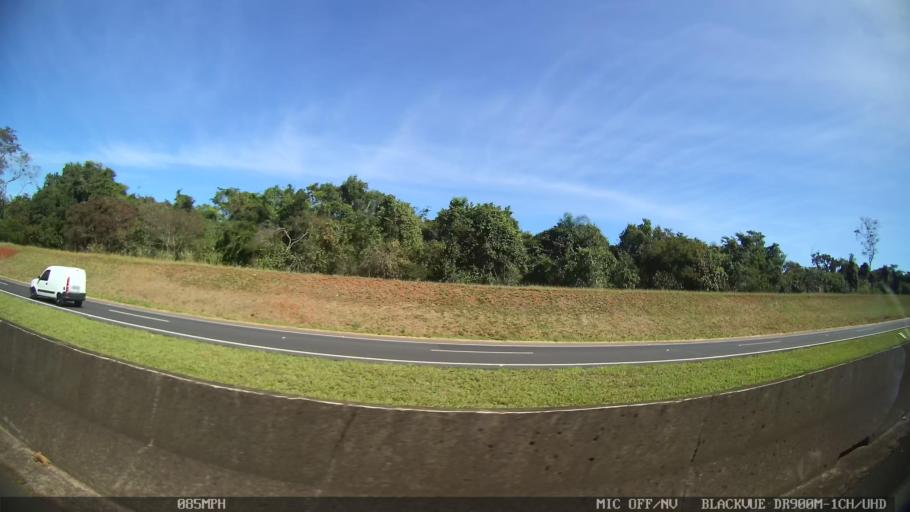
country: BR
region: Sao Paulo
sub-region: Pirassununga
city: Pirassununga
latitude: -21.9415
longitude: -47.4651
